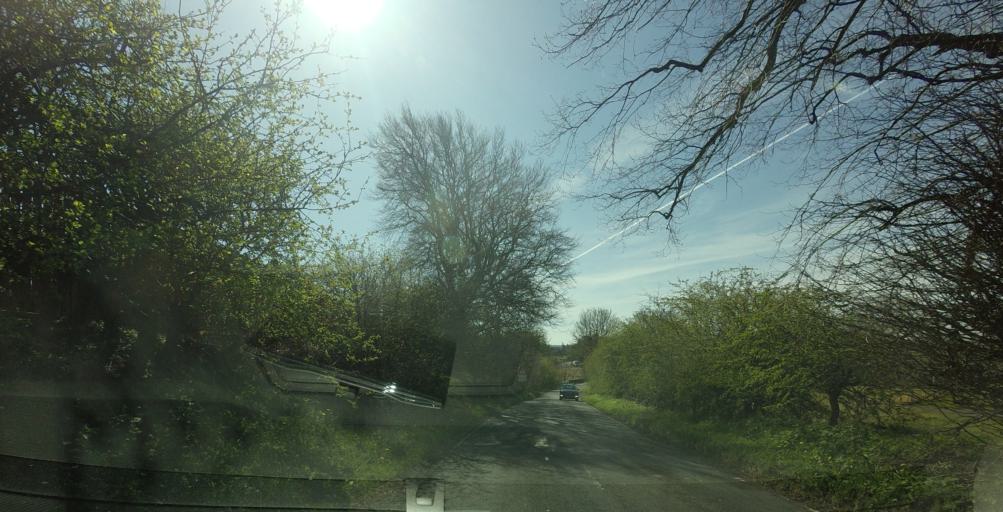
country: GB
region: Scotland
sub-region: West Lothian
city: Blackburn
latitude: 55.8699
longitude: -3.6093
